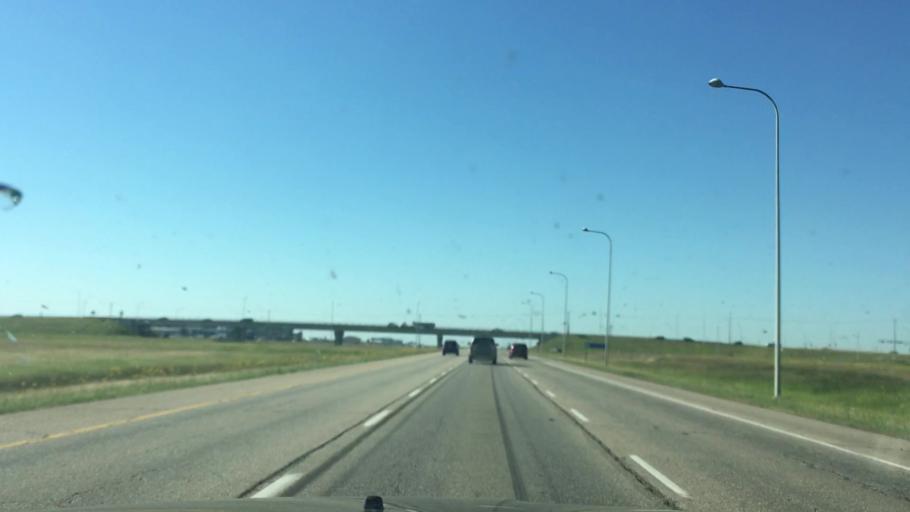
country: CA
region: Alberta
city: Leduc
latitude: 53.3124
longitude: -113.5498
